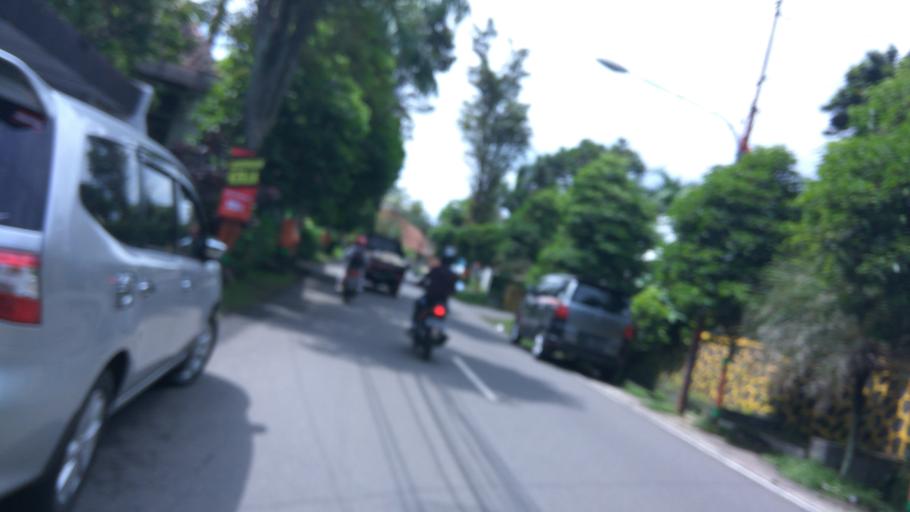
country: ID
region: Central Java
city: Ungaran
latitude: -7.1290
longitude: 110.4054
